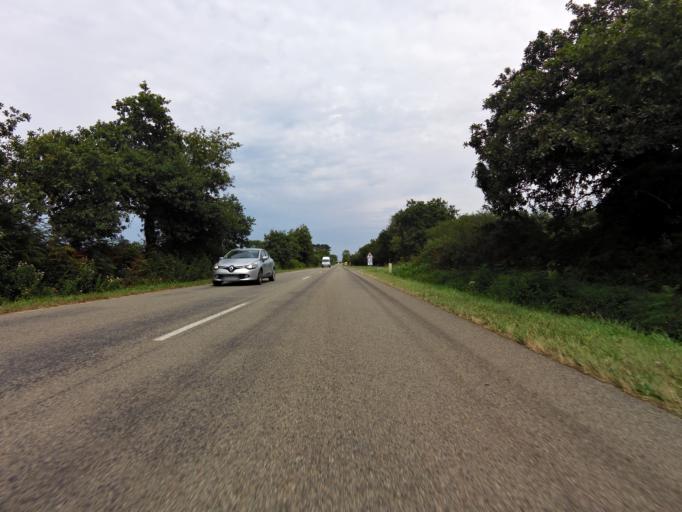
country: FR
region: Brittany
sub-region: Departement du Finistere
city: Poullan-sur-Mer
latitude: 48.0785
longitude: -4.4427
